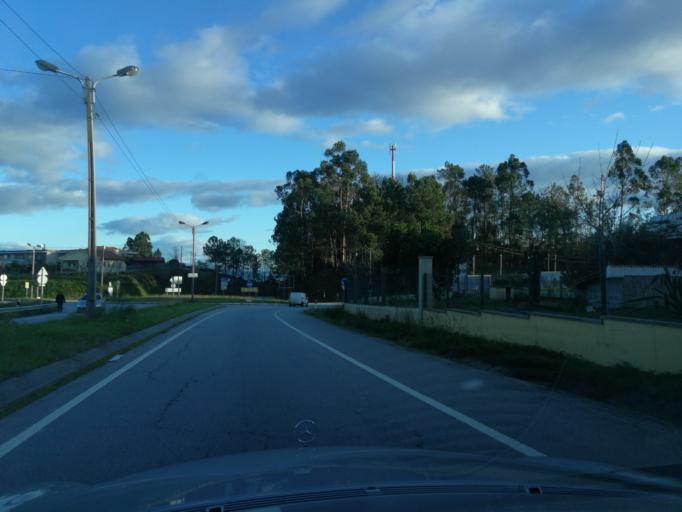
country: PT
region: Braga
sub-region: Barcelos
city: Vila Frescainha
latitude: 41.5628
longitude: -8.6595
